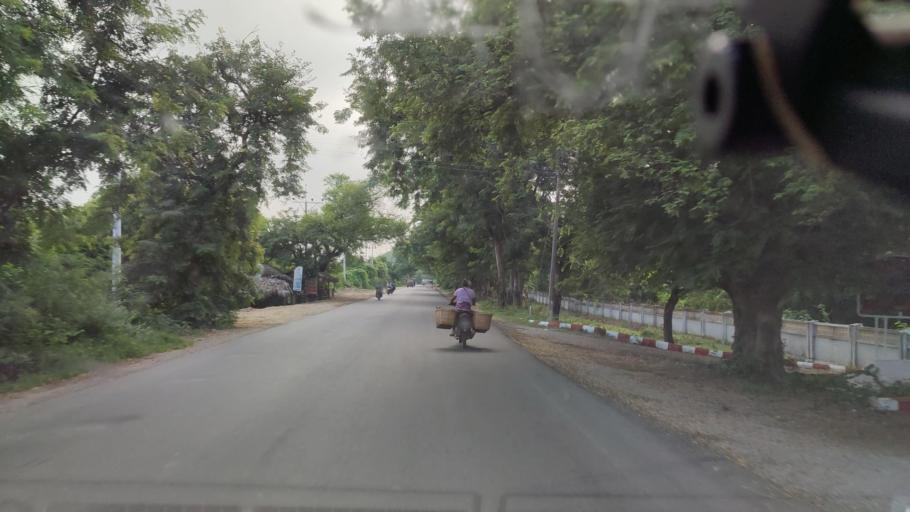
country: MM
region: Mandalay
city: Mandalay
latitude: 22.1116
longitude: 96.1549
